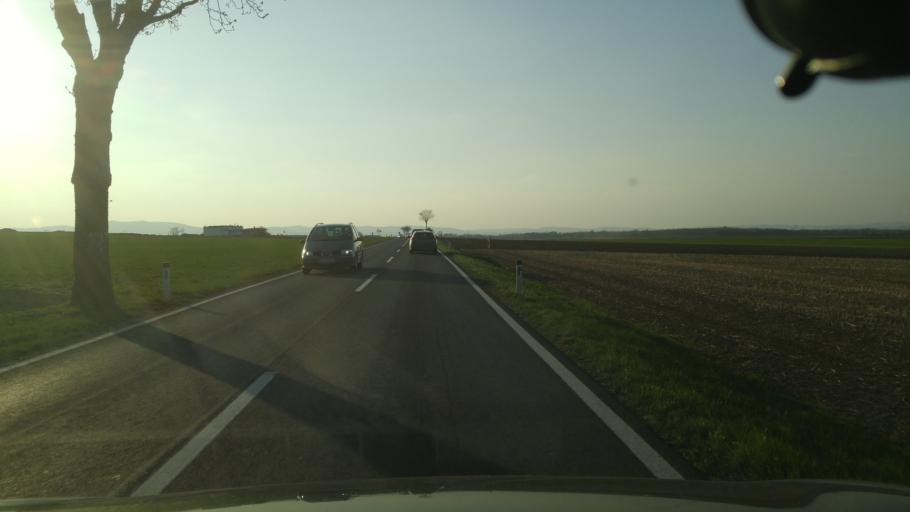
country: AT
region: Lower Austria
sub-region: Politischer Bezirk Wien-Umgebung
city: Gramatneusiedl
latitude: 48.0390
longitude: 16.4743
